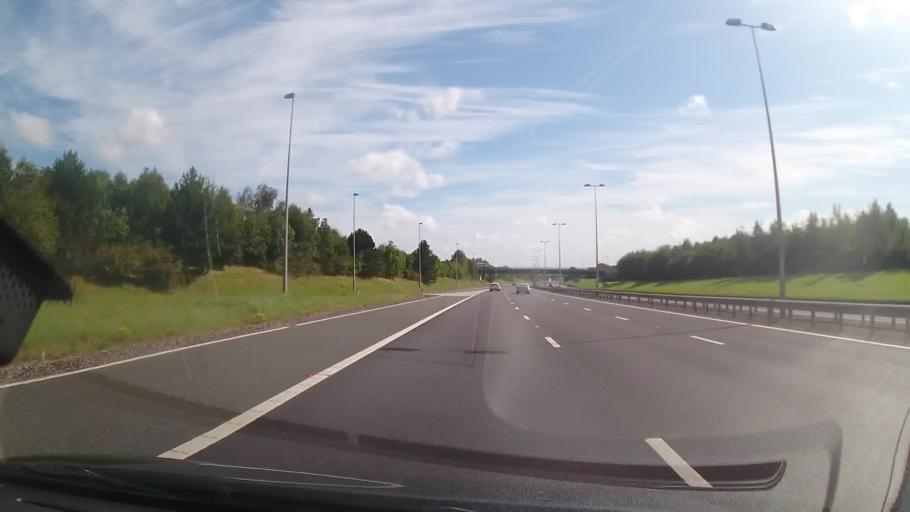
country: GB
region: England
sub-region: Staffordshire
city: Chasetown
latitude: 52.6626
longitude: -1.9254
